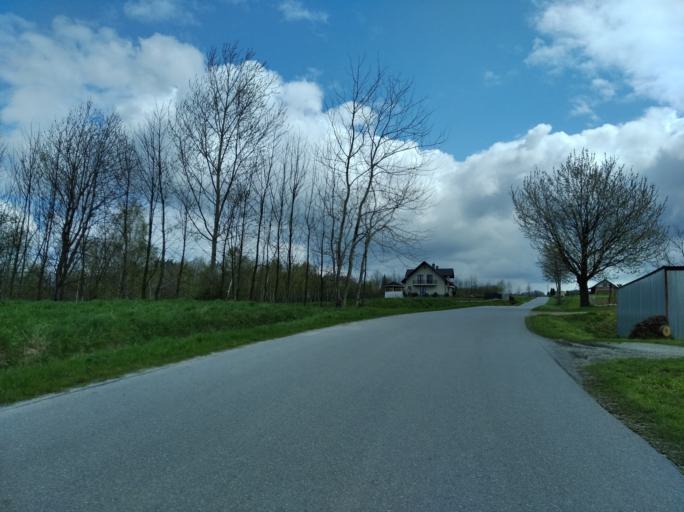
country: PL
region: Subcarpathian Voivodeship
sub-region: Powiat strzyzowski
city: Polomia
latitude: 49.8851
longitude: 21.9090
